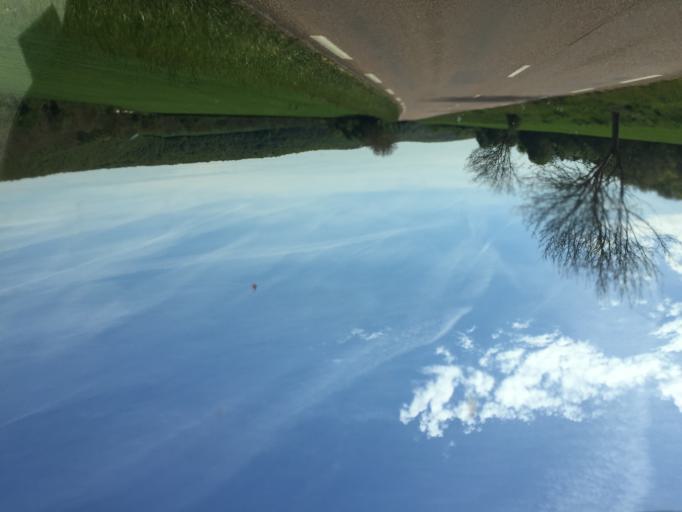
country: FR
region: Bourgogne
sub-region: Departement de la Nievre
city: Clamecy
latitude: 47.4399
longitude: 3.5583
